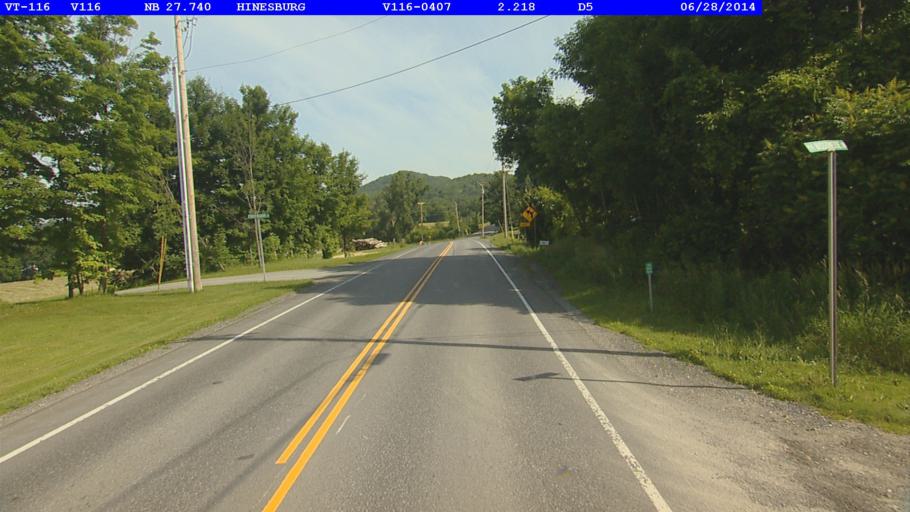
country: US
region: Vermont
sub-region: Chittenden County
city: Hinesburg
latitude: 44.3115
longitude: -73.0758
